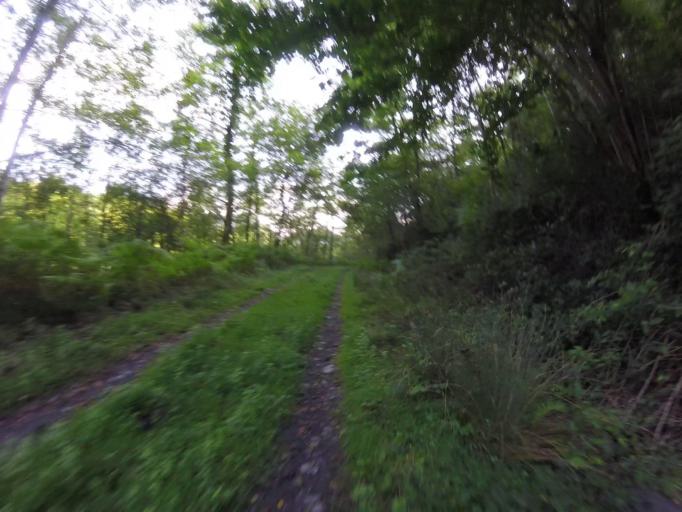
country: ES
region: Navarre
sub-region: Provincia de Navarra
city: Arano
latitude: 43.2279
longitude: -1.9114
